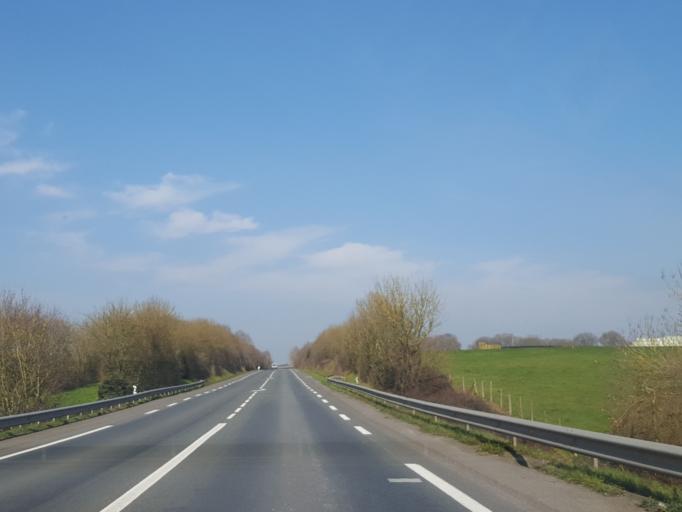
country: FR
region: Pays de la Loire
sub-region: Departement de la Vendee
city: Saint-Fulgent
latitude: 46.8390
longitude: -1.1620
